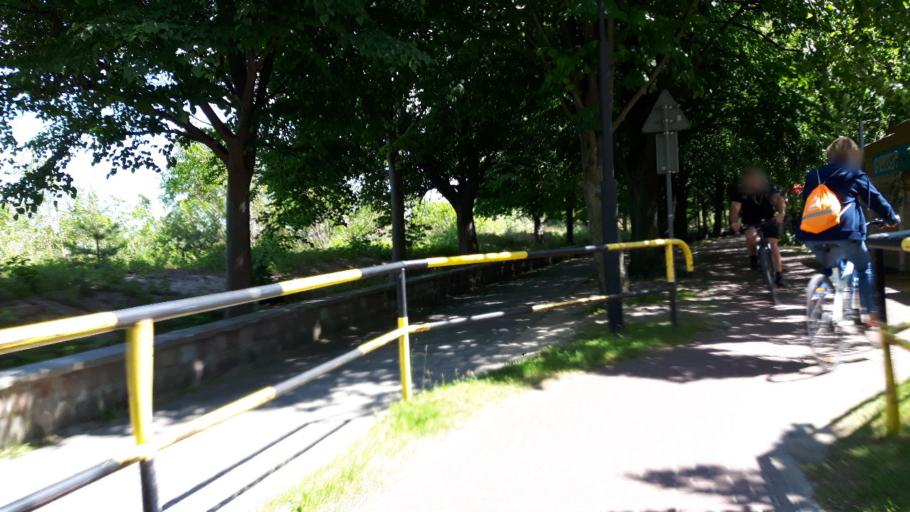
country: PL
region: Pomeranian Voivodeship
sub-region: Sopot
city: Sopot
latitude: 54.4324
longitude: 18.5872
